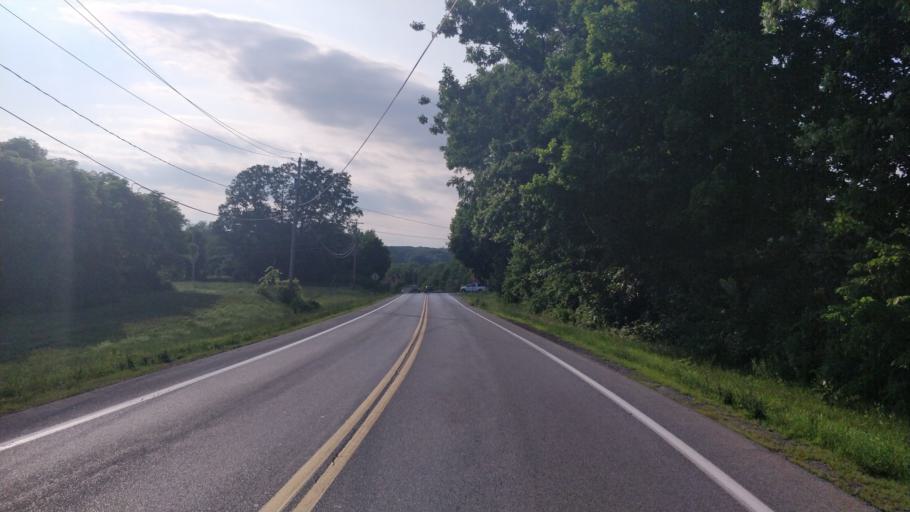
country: US
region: New York
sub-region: Saratoga County
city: North Ballston Spa
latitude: 43.0176
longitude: -73.8228
